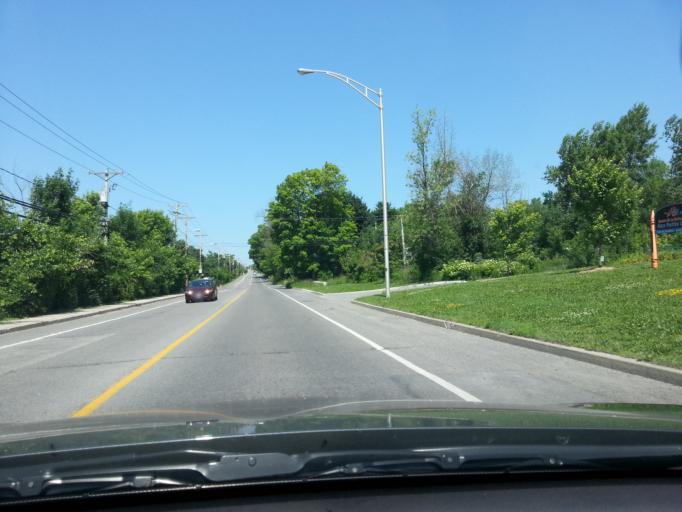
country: CA
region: Ontario
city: Bells Corners
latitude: 45.4024
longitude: -75.8562
